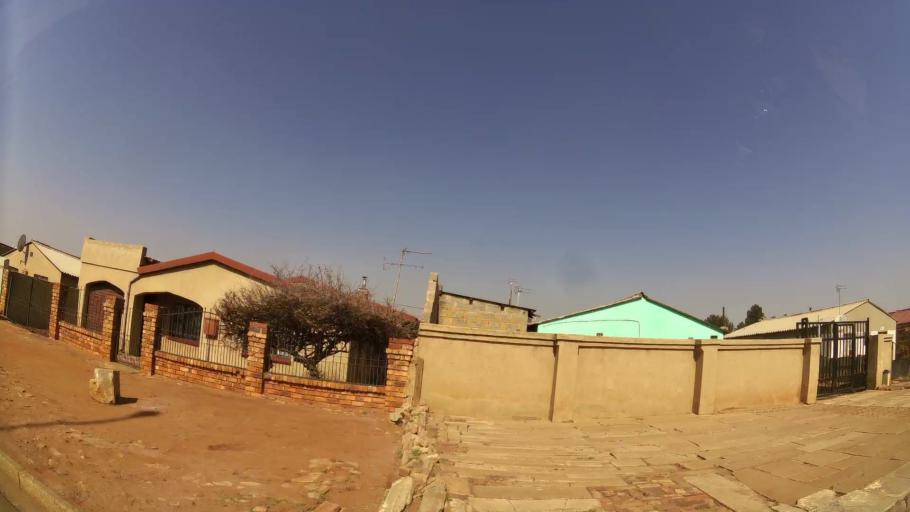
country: ZA
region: Gauteng
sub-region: Ekurhuleni Metropolitan Municipality
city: Benoni
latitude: -26.2264
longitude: 28.3005
